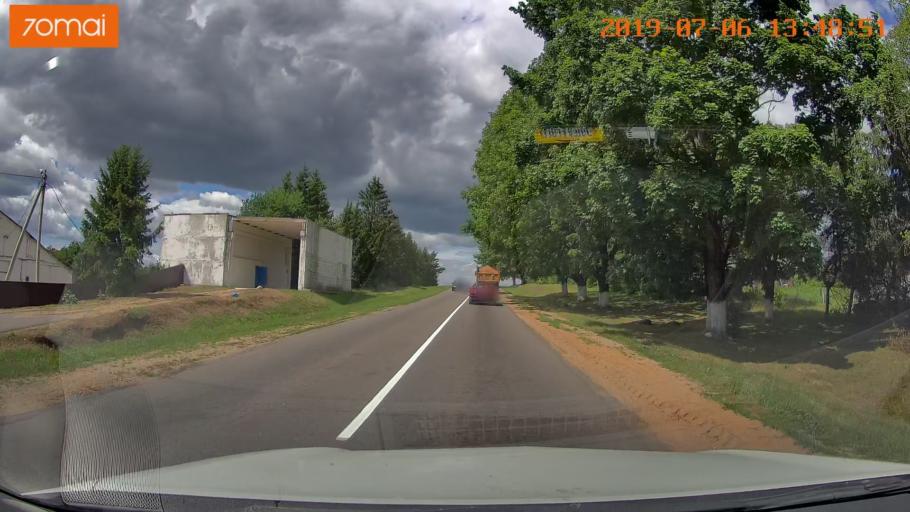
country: BY
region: Minsk
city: Ivyanyets
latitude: 53.6918
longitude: 26.8547
